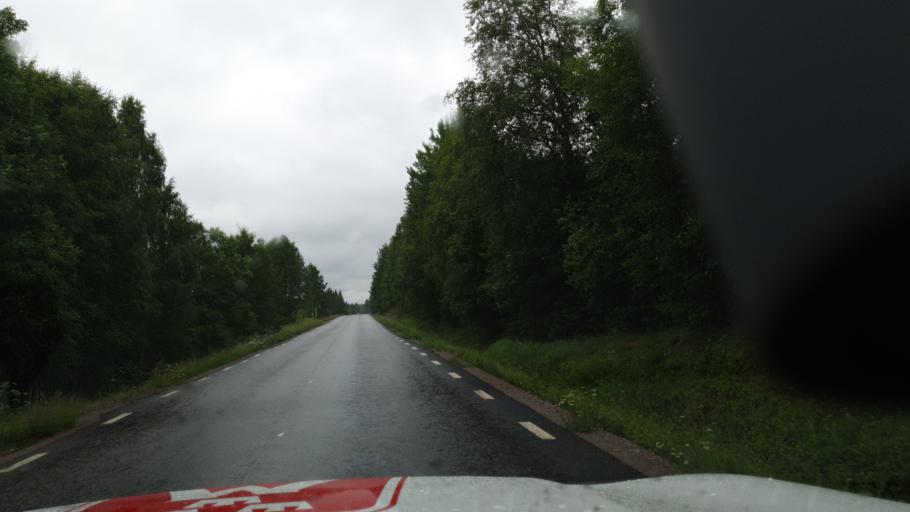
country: SE
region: Vaesterbotten
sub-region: Vannas Kommun
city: Vannasby
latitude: 63.8290
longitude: 19.8572
